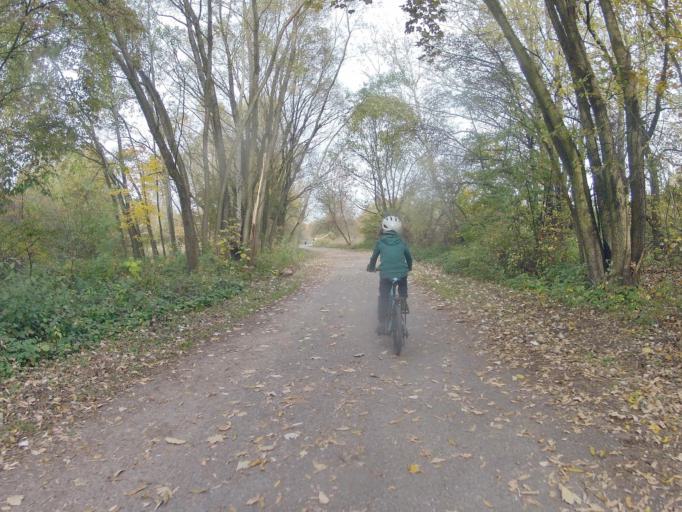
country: PL
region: Lesser Poland Voivodeship
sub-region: Krakow
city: Krakow
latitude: 50.0378
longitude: 19.9154
